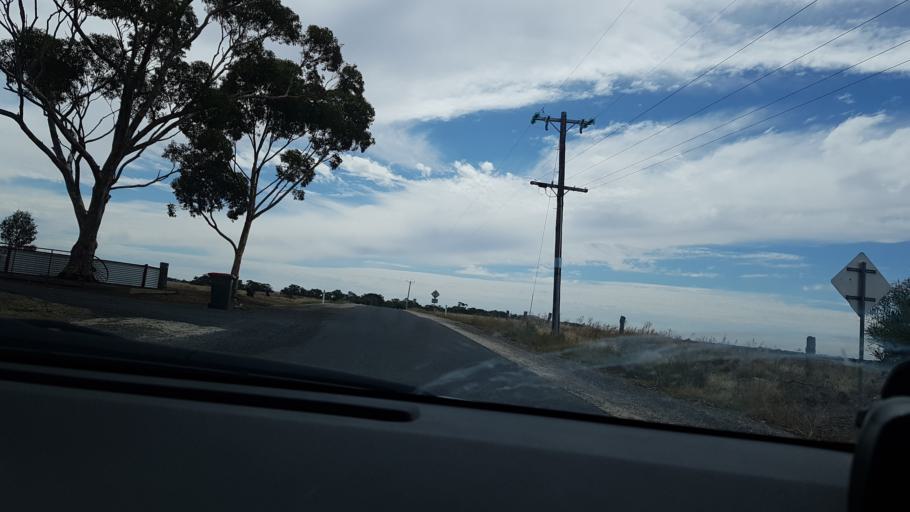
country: AU
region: Victoria
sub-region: Horsham
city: Horsham
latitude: -36.7266
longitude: 141.7814
